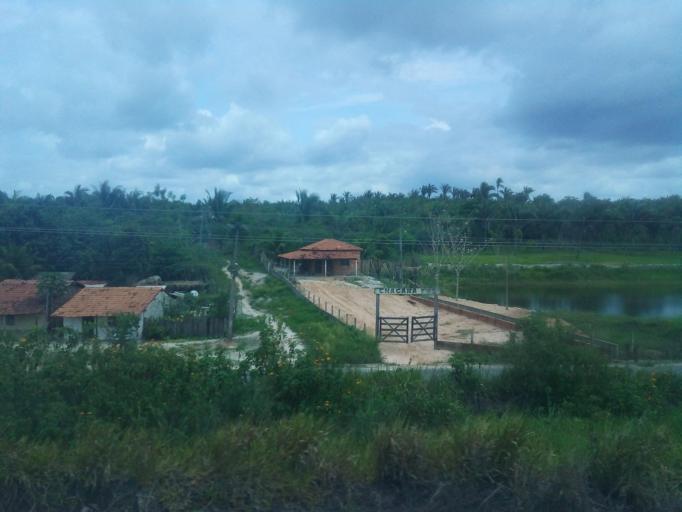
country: BR
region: Maranhao
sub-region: Santa Ines
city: Santa Ines
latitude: -3.7015
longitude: -45.9290
